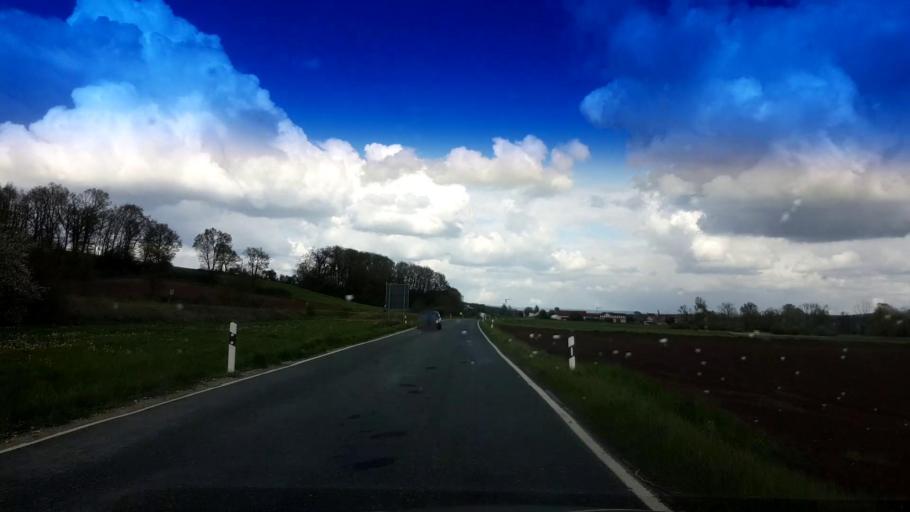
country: DE
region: Bavaria
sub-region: Upper Franconia
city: Frensdorf
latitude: 49.7844
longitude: 10.8497
